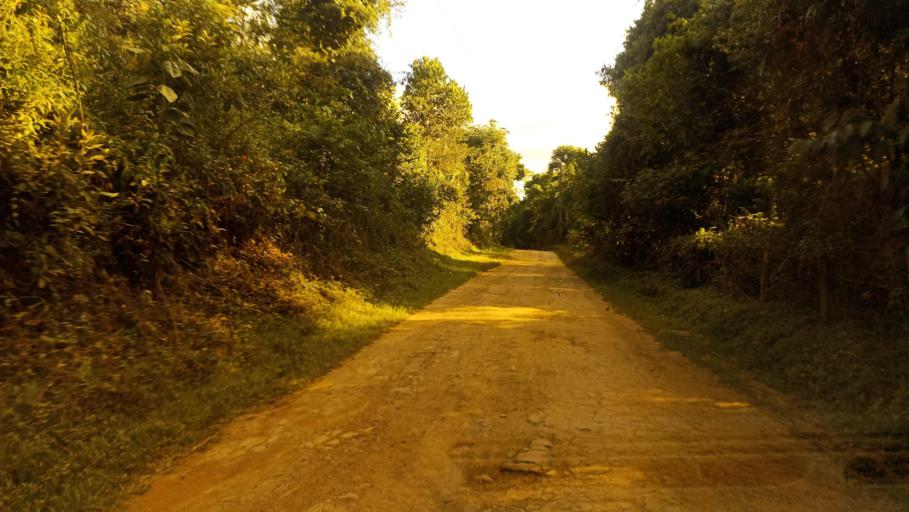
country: BR
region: Minas Gerais
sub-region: Ouro Preto
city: Ouro Preto
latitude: -20.3053
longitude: -43.5765
